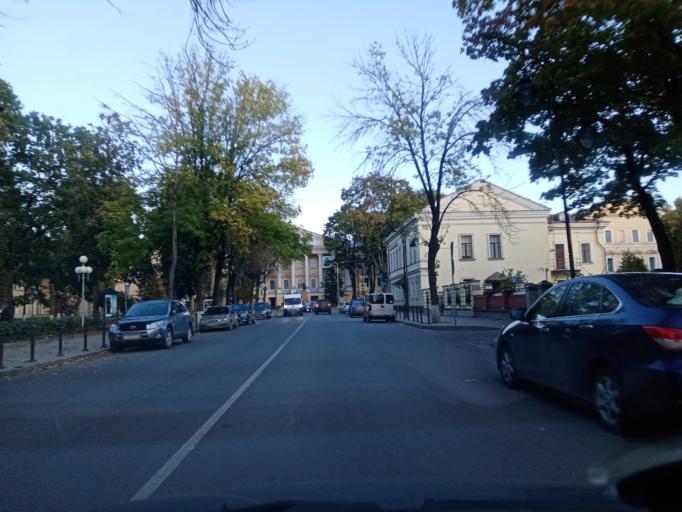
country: RU
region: Pskov
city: Pskov
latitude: 57.8165
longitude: 28.3401
